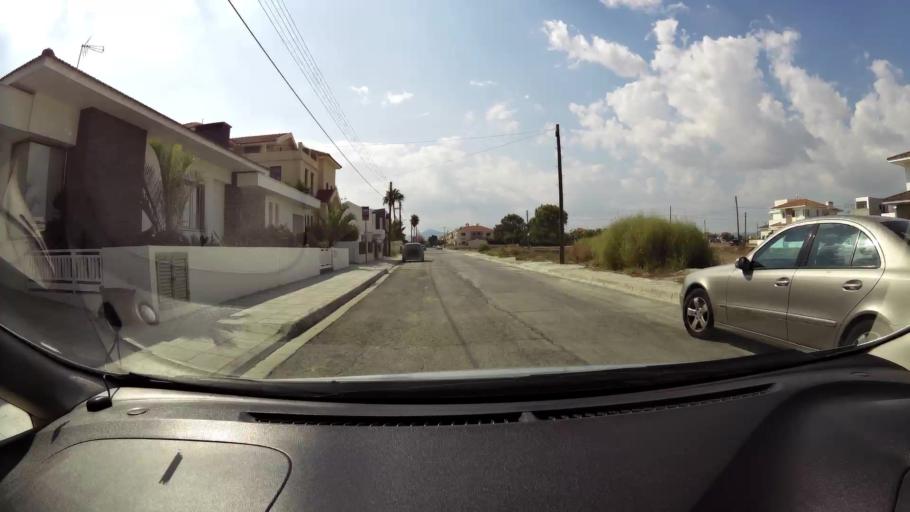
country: CY
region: Larnaka
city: Dhromolaxia
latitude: 34.9075
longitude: 33.5908
